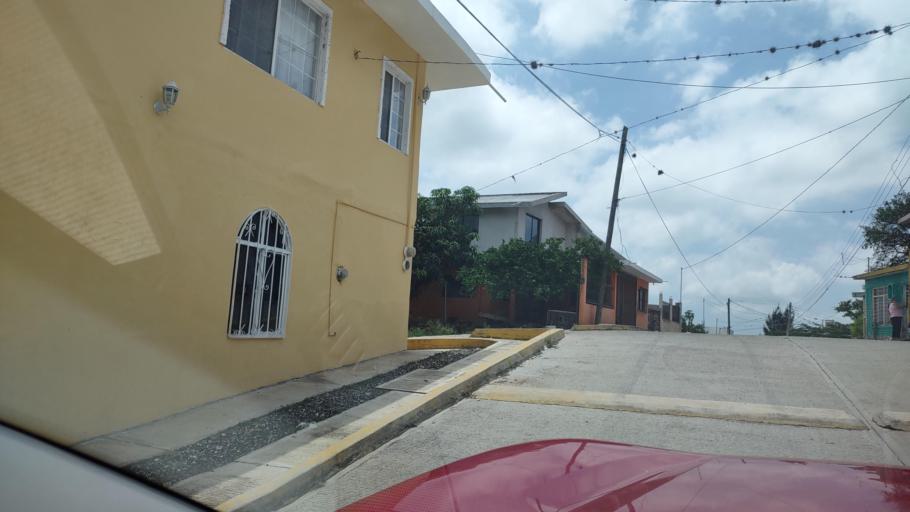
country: MX
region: Veracruz
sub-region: Emiliano Zapata
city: Dos Rios
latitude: 19.4880
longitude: -96.8142
